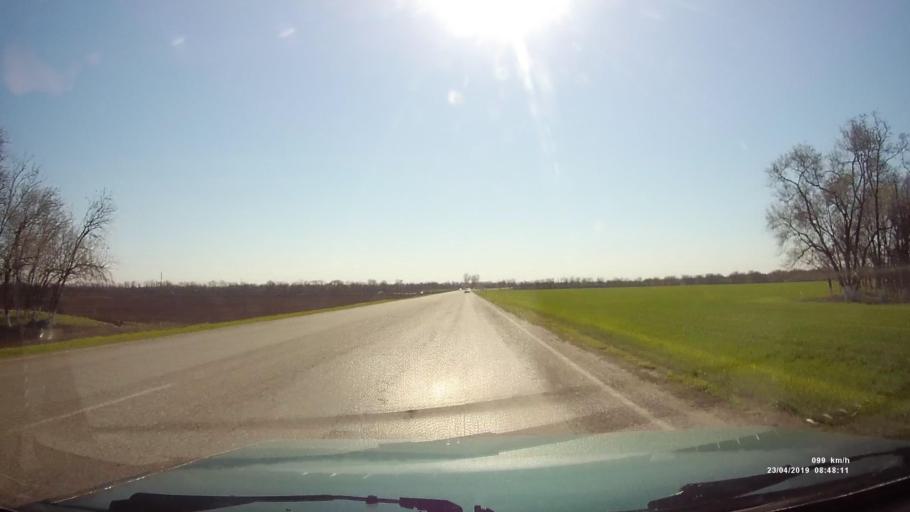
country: RU
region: Rostov
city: Gigant
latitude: 46.5120
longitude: 41.3874
